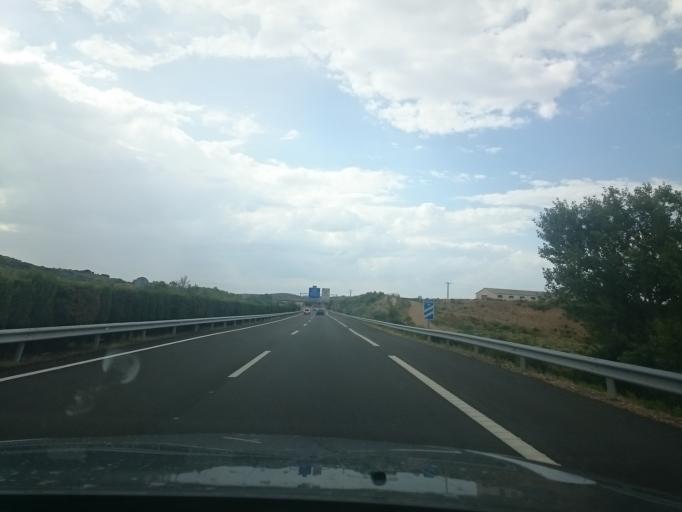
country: ES
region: Navarre
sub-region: Provincia de Navarra
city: Sartaguda
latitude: 42.3658
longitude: -2.0720
